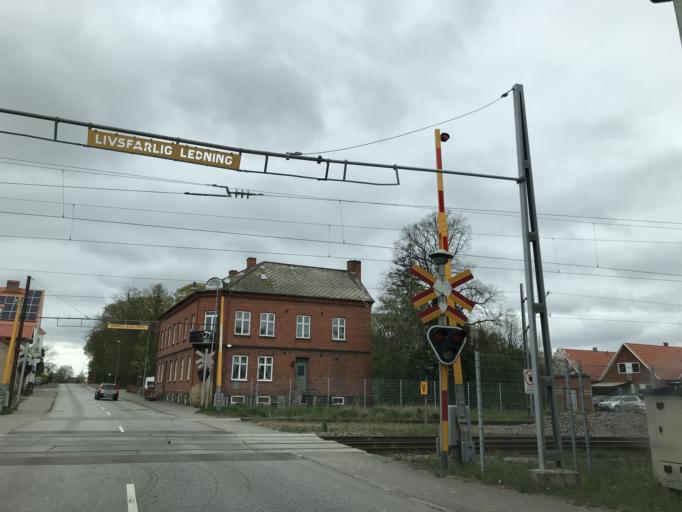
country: SE
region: Skane
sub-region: Svalovs Kommun
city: Teckomatorp
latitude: 55.8705
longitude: 13.0883
